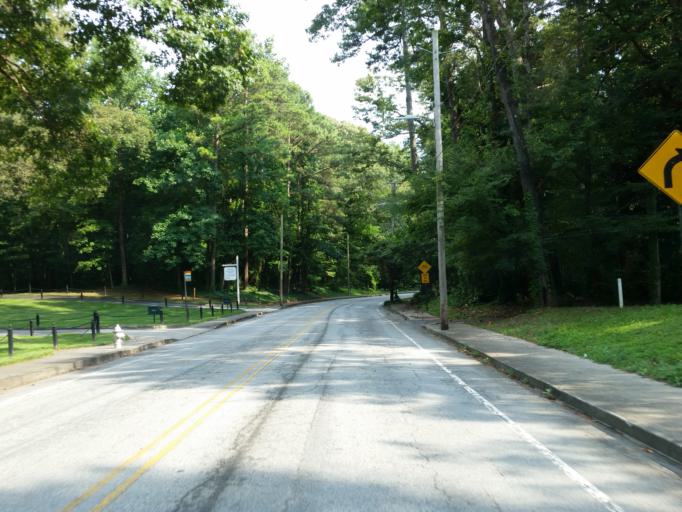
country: US
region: Georgia
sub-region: Cobb County
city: Vinings
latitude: 33.8371
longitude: -84.4201
